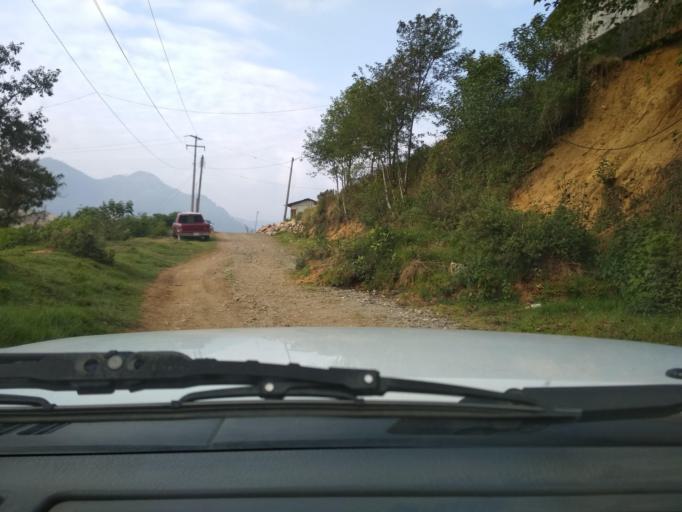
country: MX
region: Veracruz
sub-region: Soledad Atzompa
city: Tlatilpa
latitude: 18.7544
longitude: -97.1572
